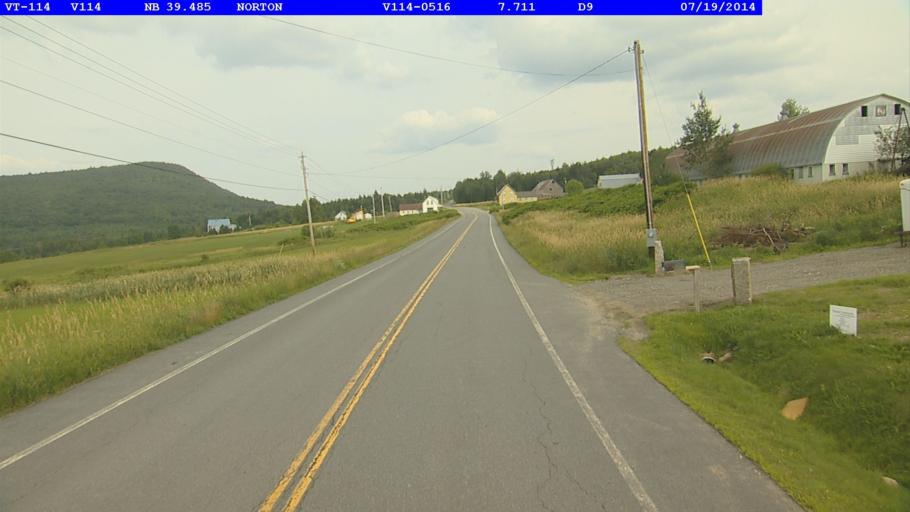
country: CA
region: Quebec
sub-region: Estrie
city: Coaticook
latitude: 44.9995
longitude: -71.7507
